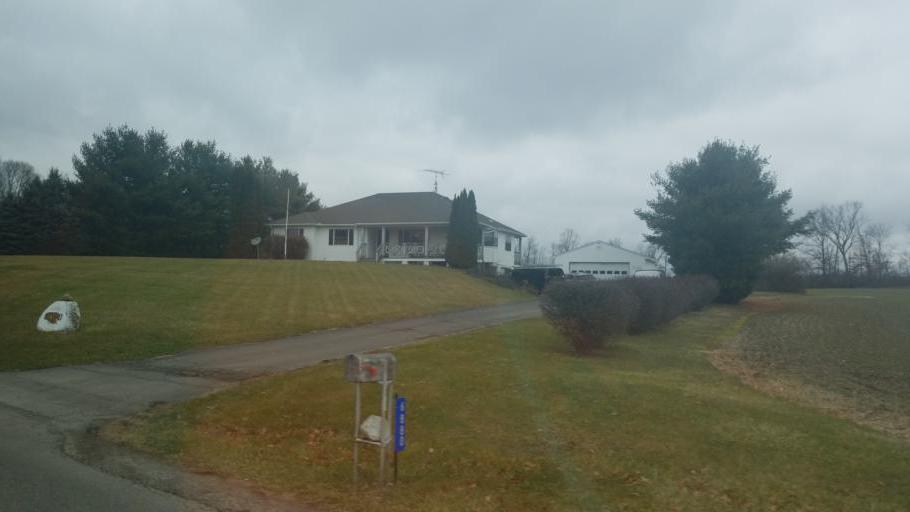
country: US
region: Ohio
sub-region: Crawford County
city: Galion
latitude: 40.7727
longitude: -82.7879
